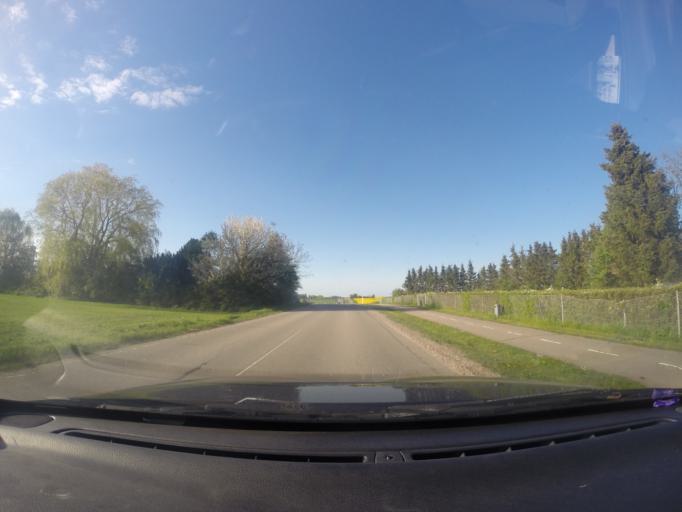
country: DK
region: Capital Region
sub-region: Hoje-Taastrup Kommune
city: Taastrup
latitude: 55.6688
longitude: 12.2537
